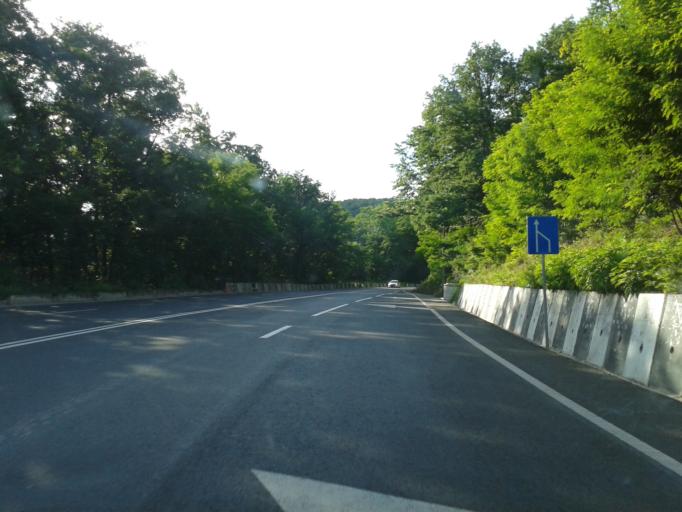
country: RO
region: Hunedoara
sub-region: Comuna Santamaria-Orlea
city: Santamaria-Orlea
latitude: 45.6132
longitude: 22.9766
